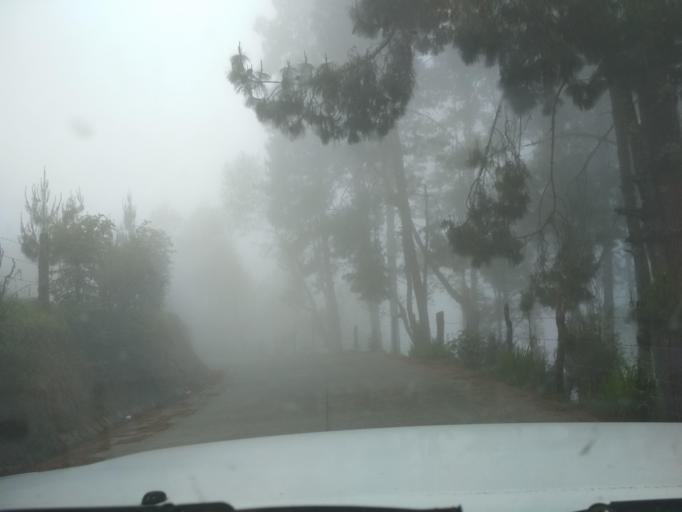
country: MX
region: Veracruz
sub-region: La Perla
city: Chilapa
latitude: 18.9809
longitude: -97.1871
